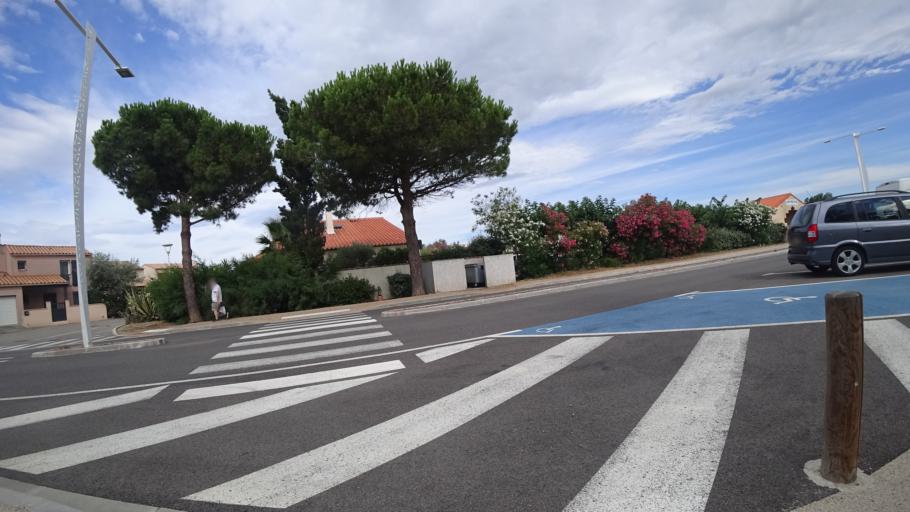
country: FR
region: Languedoc-Roussillon
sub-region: Departement des Pyrenees-Orientales
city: Le Barcares
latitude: 42.8444
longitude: 3.0371
